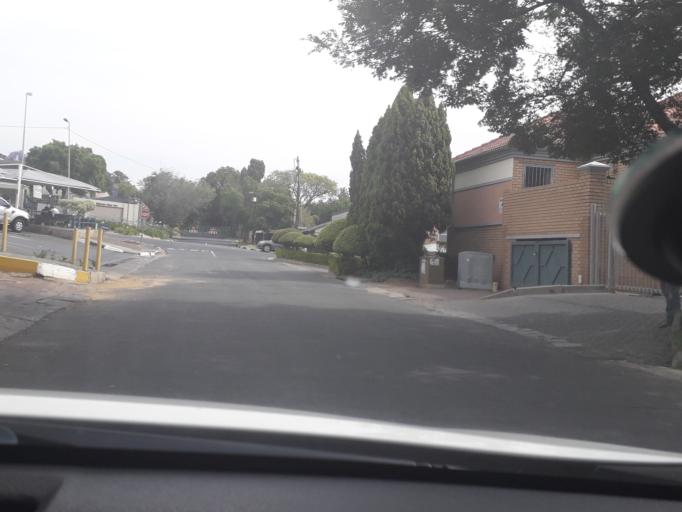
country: ZA
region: Gauteng
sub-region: City of Johannesburg Metropolitan Municipality
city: Johannesburg
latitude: -26.0988
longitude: 27.9974
